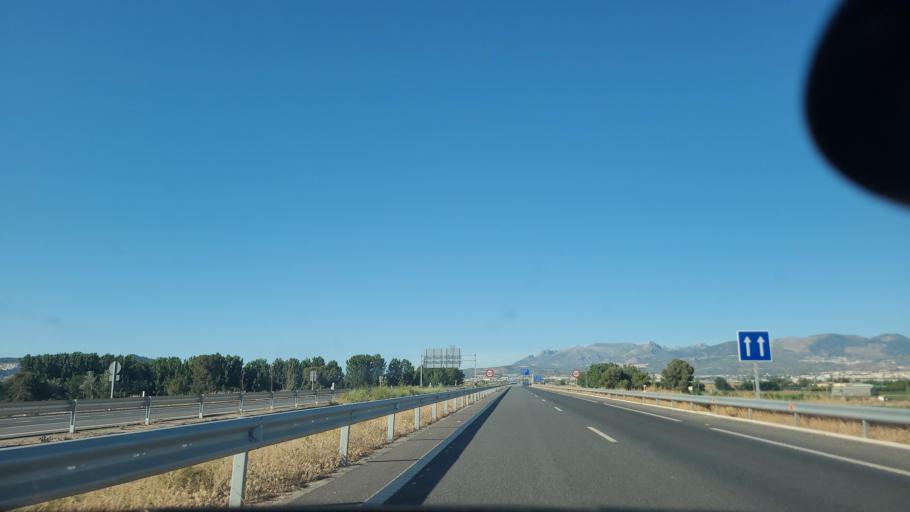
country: ES
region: Andalusia
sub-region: Provincia de Granada
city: Atarfe
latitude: 37.1880
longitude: -3.6935
